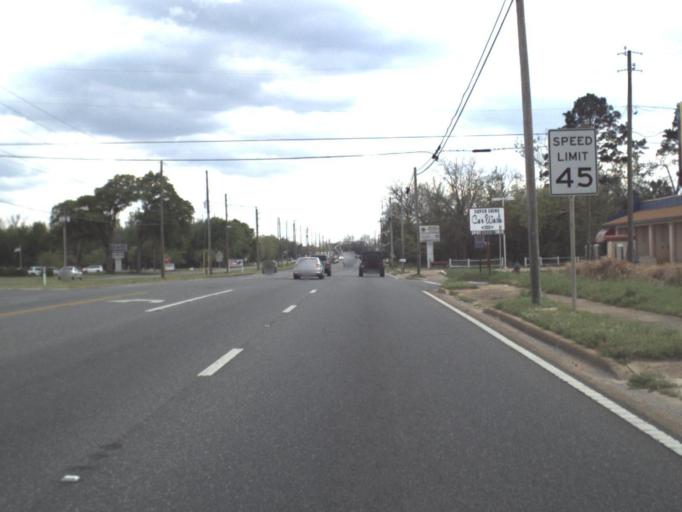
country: US
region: Florida
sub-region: Okaloosa County
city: Crestview
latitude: 30.7854
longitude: -86.5597
